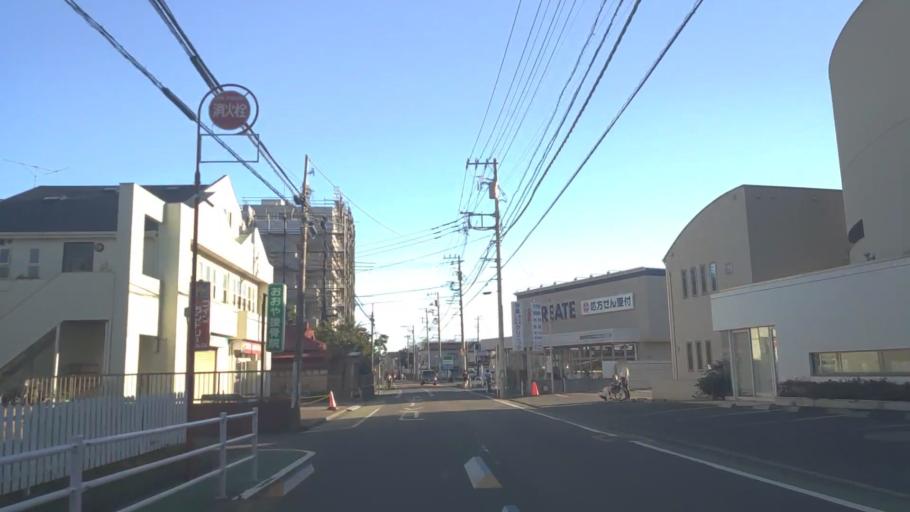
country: JP
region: Kanagawa
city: Chigasaki
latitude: 35.3306
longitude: 139.4145
